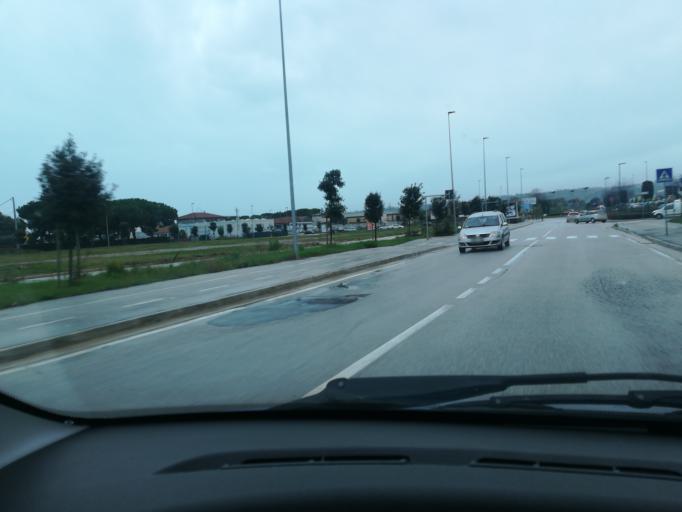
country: IT
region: The Marches
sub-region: Provincia di Macerata
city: Santa Maria Apparente
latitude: 43.2955
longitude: 13.7020
